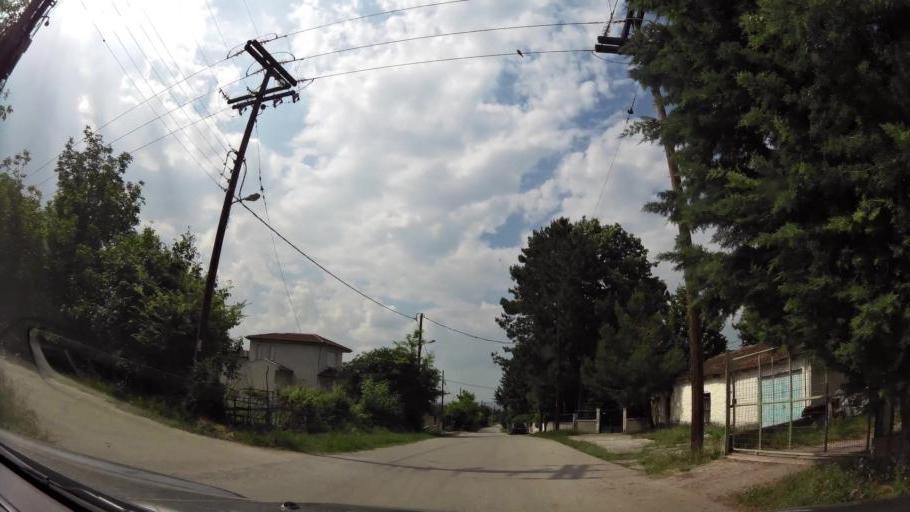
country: GR
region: West Macedonia
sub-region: Nomos Kozanis
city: Koila
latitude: 40.3488
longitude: 21.8388
